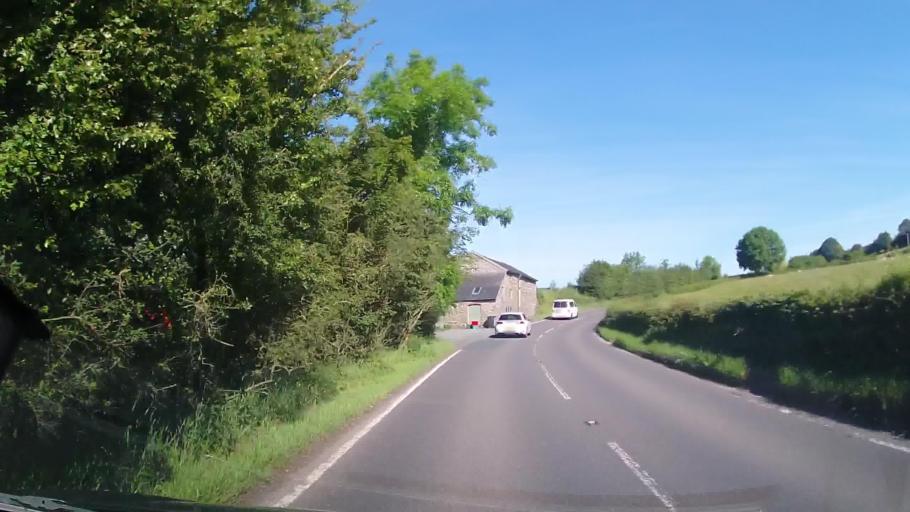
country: GB
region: Wales
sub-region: Sir Powys
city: Welshpool
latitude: 52.6546
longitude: -3.2574
